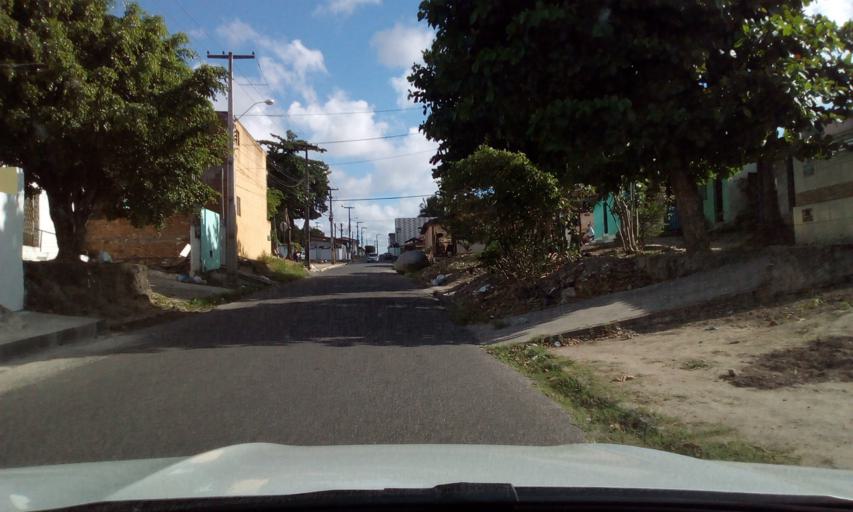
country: BR
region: Paraiba
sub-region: Bayeux
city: Bayeux
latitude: -7.1725
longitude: -34.8953
